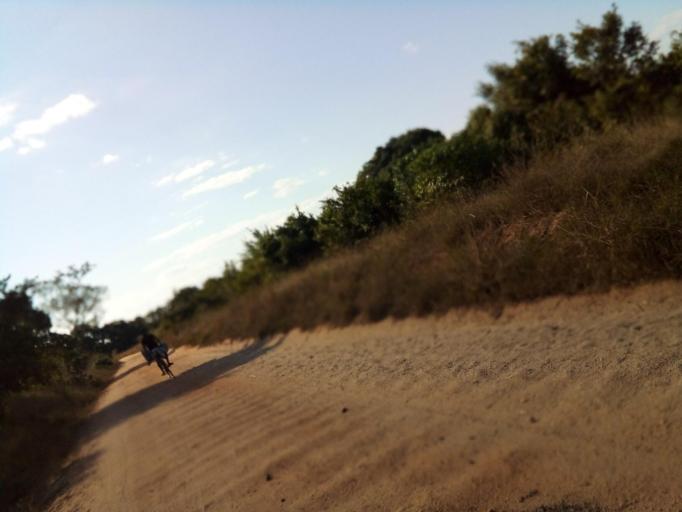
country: MZ
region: Zambezia
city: Quelimane
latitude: -17.5453
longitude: 36.6273
